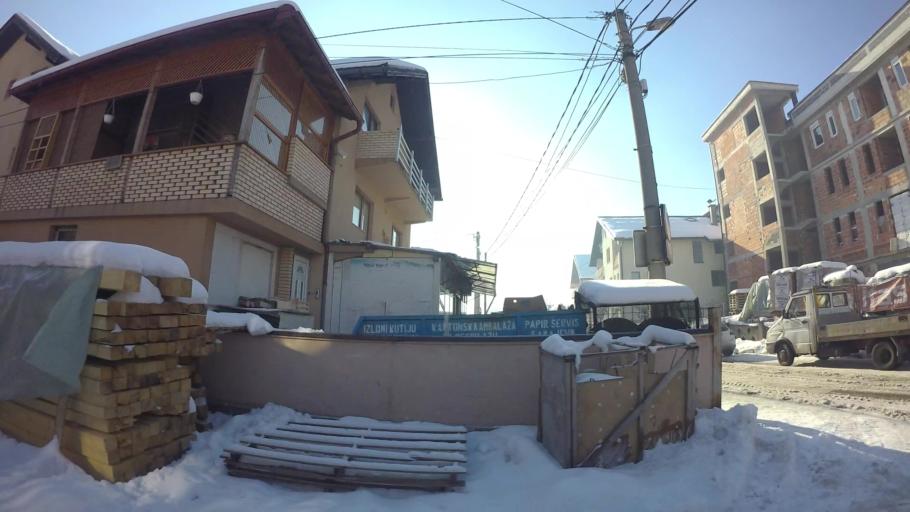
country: BA
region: Federation of Bosnia and Herzegovina
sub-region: Kanton Sarajevo
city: Sarajevo
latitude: 43.8097
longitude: 18.3154
